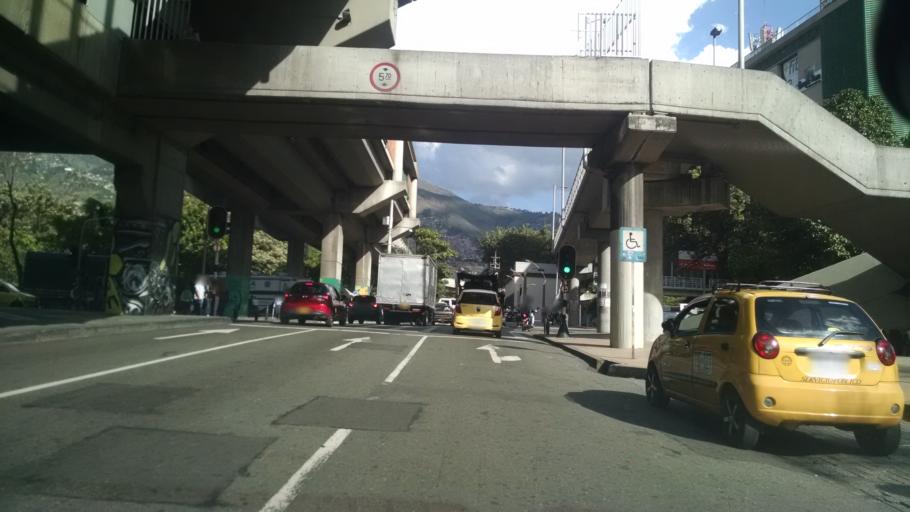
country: CO
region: Antioquia
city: Medellin
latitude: 6.2694
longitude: -75.5659
